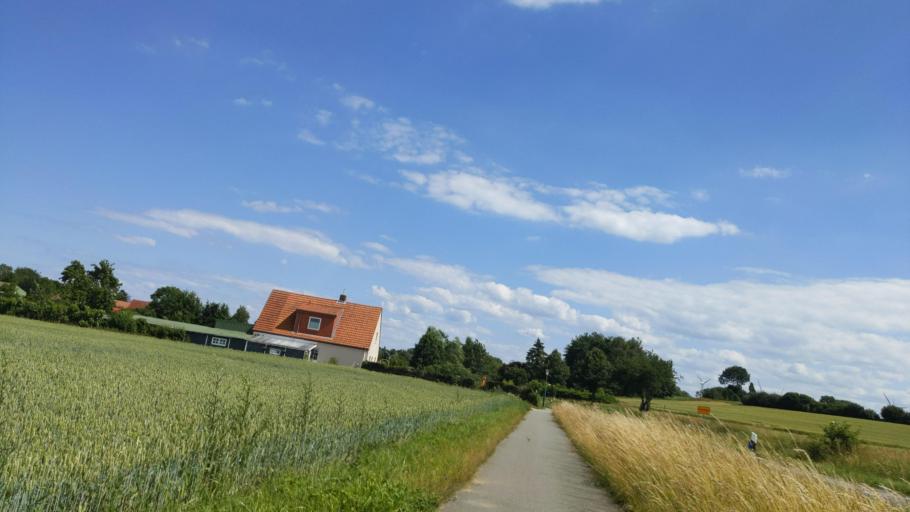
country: DE
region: Schleswig-Holstein
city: Schashagen
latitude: 54.1620
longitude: 10.9048
